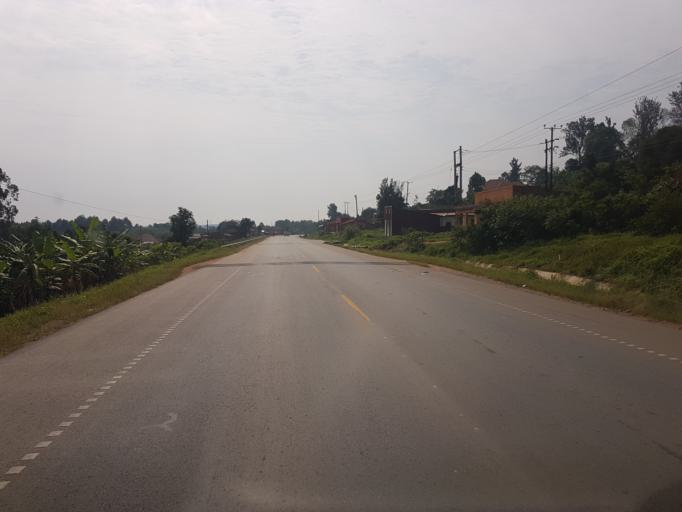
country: UG
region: Western Region
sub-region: Sheema District
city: Kibingo
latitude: -0.6363
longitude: 30.5175
